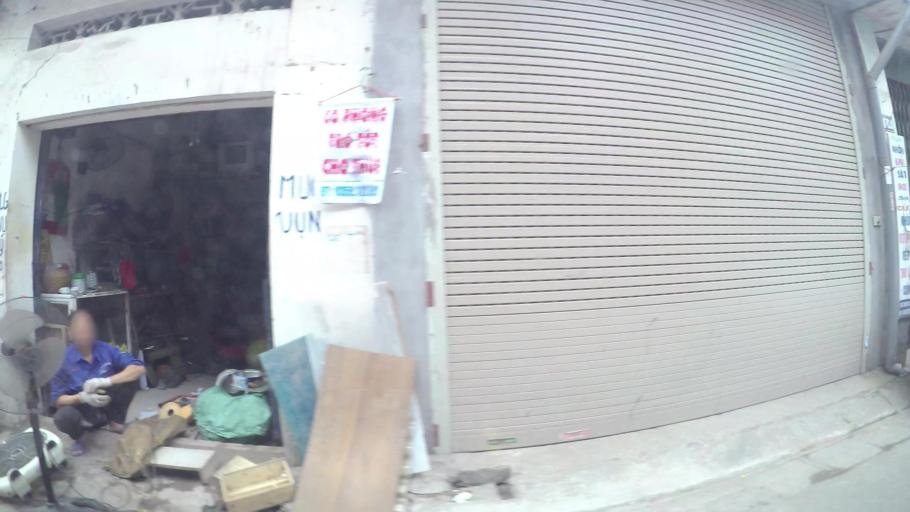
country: VN
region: Ha Noi
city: Hai BaTrung
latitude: 20.9898
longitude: 105.8886
